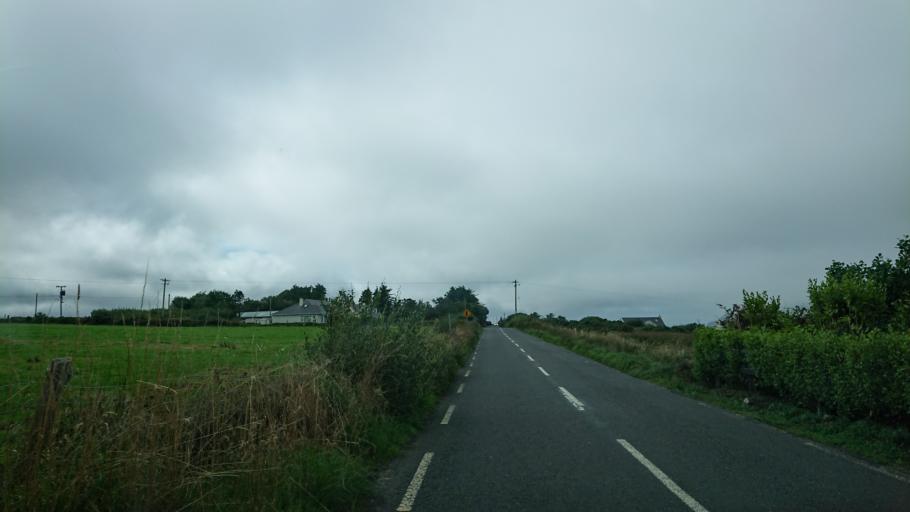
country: IE
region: Munster
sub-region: Ciarrai
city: Cahersiveen
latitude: 51.9324
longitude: -10.2492
